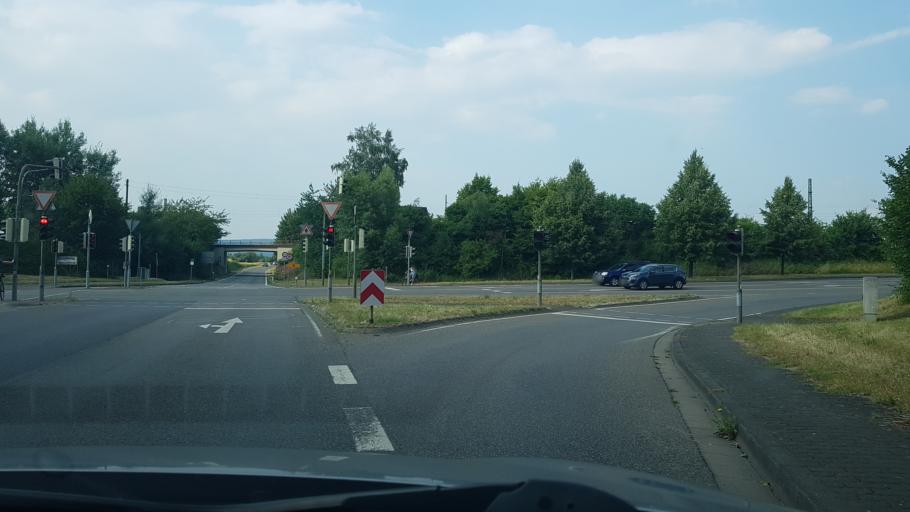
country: DE
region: Rheinland-Pfalz
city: Kaltenengers
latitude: 50.3955
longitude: 7.5389
